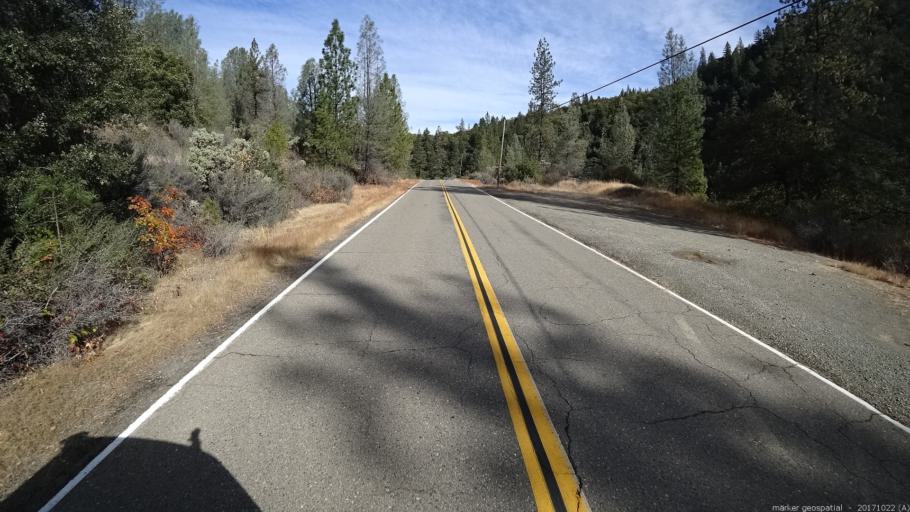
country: US
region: California
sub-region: Siskiyou County
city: Dunsmuir
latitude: 41.0080
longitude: -122.4079
